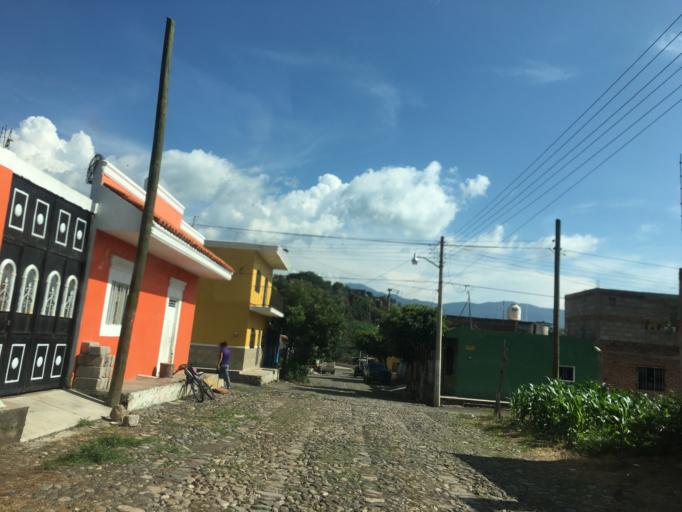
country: MX
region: Nayarit
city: Ixtlan del Rio
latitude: 21.0448
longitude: -104.3605
